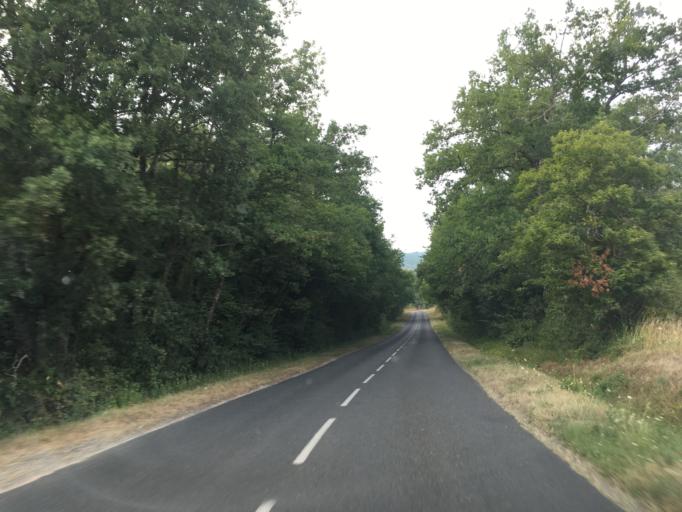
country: FR
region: Midi-Pyrenees
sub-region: Departement du Lot
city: Souillac
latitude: 44.8466
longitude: 1.5429
